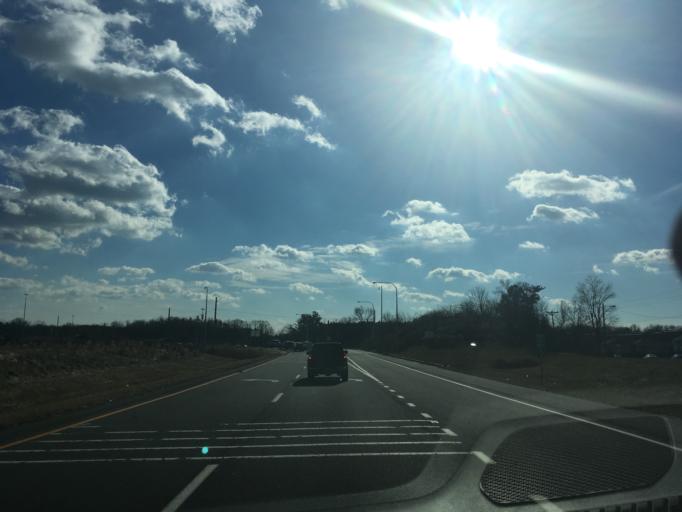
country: US
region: Delaware
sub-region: New Castle County
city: Bear
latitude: 39.6773
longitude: -75.6573
